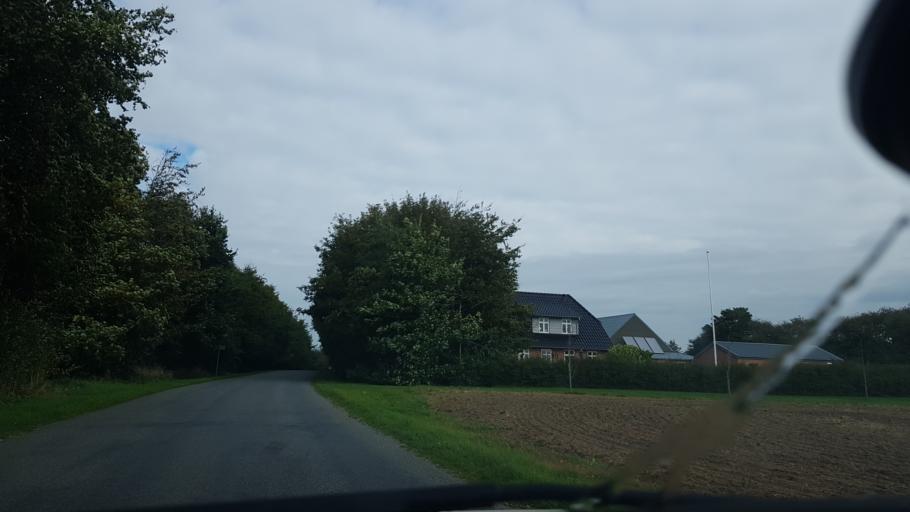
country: DK
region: South Denmark
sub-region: Vejen Kommune
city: Brorup
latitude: 55.4685
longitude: 8.9695
